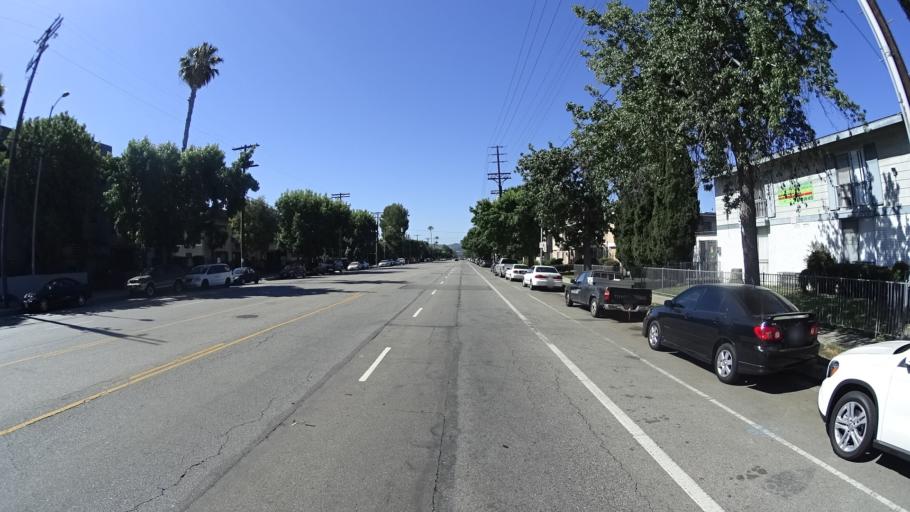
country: US
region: California
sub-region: Los Angeles County
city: Van Nuys
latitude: 34.1928
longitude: -118.4837
